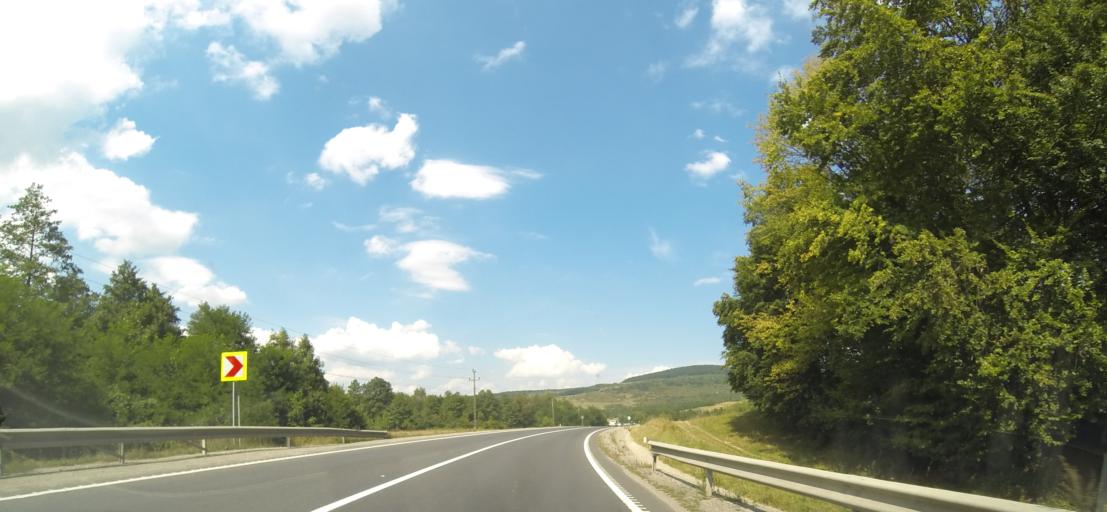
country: RO
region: Brasov
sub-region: Comuna Sinca Veche
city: Persani
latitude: 45.7642
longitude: 25.2314
